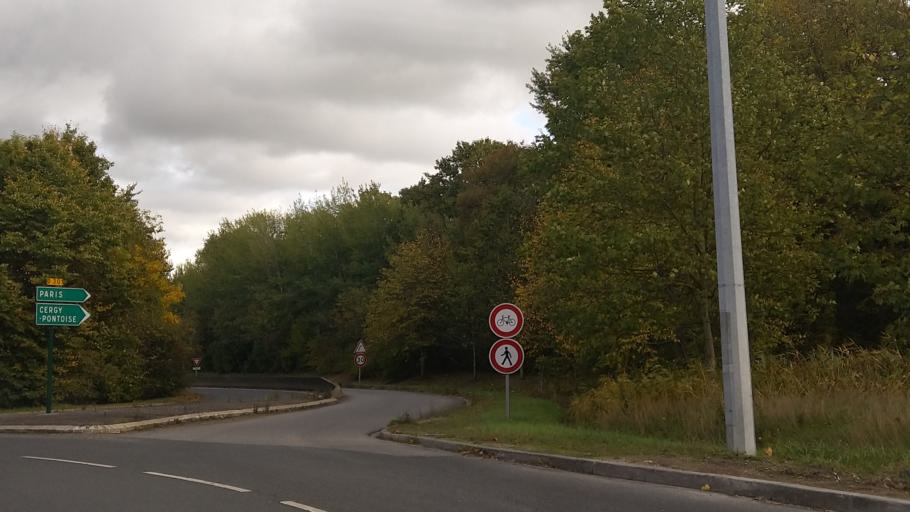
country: FR
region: Ile-de-France
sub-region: Departement du Val-d'Oise
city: Champagne-sur-Oise
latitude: 49.1239
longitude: 2.2494
